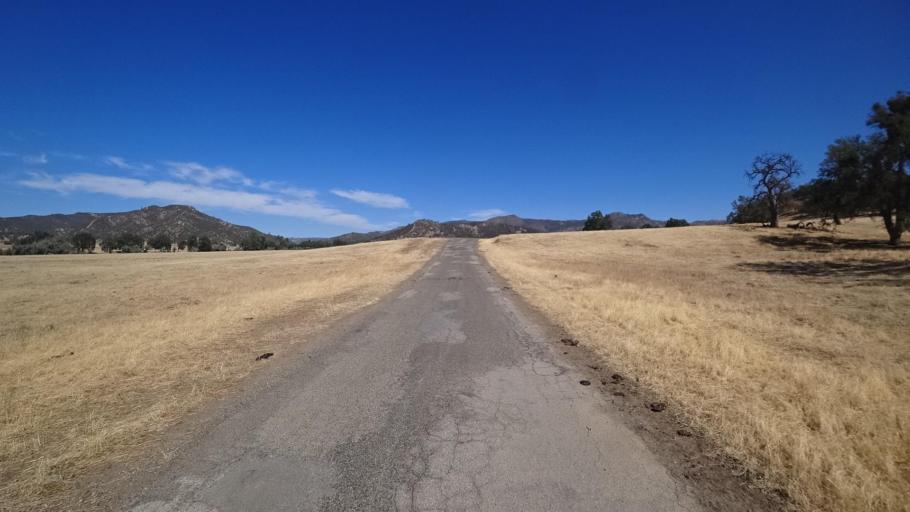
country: US
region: California
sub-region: Fresno County
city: Coalinga
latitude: 36.2039
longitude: -120.7035
